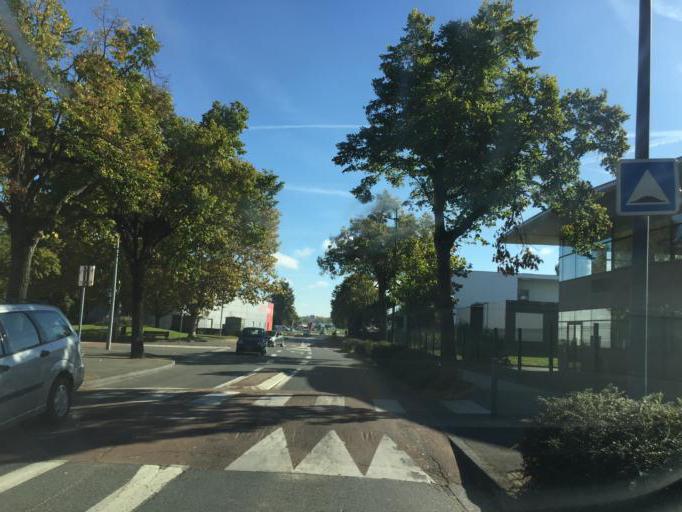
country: FR
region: Rhone-Alpes
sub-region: Departement du Rhone
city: Belleville
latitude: 46.1047
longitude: 4.7438
